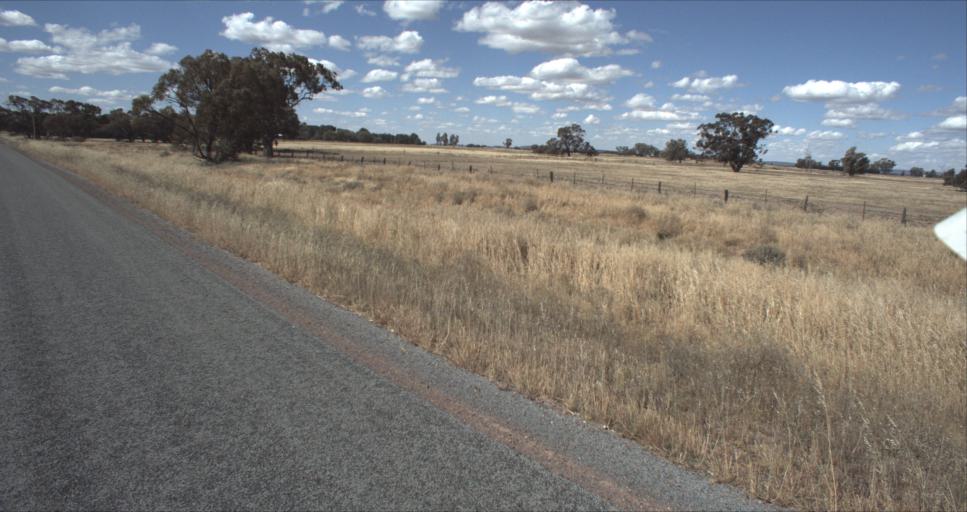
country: AU
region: New South Wales
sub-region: Leeton
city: Leeton
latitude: -34.4889
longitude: 146.2476
